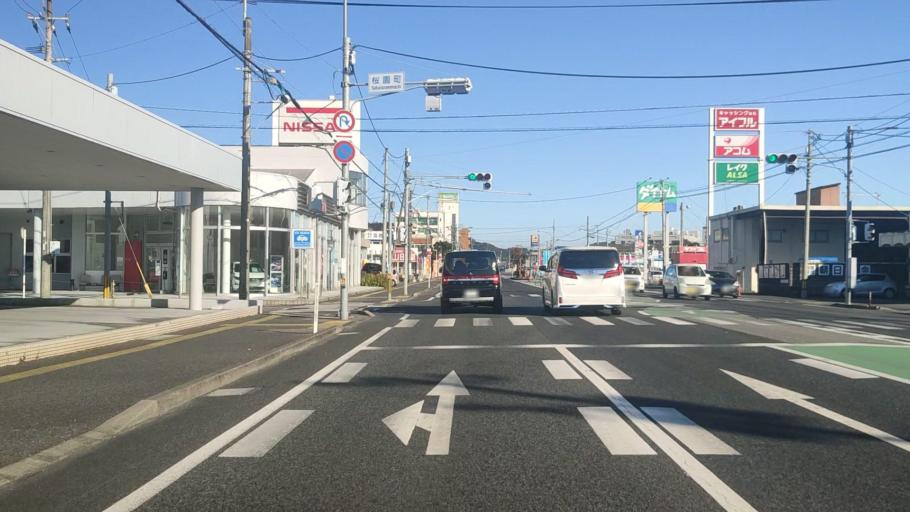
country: JP
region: Miyazaki
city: Nobeoka
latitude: 32.5932
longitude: 131.6764
